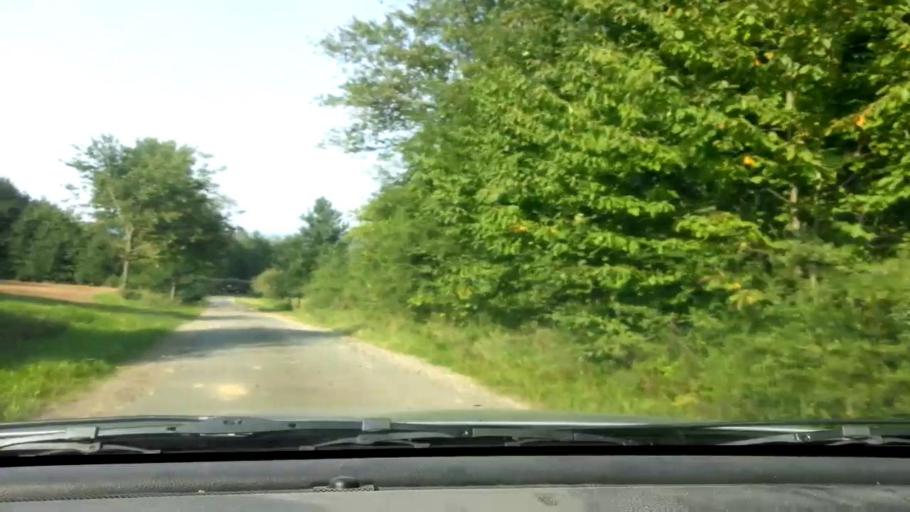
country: DE
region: Bavaria
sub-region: Upper Franconia
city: Zapfendorf
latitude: 49.9997
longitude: 10.9336
